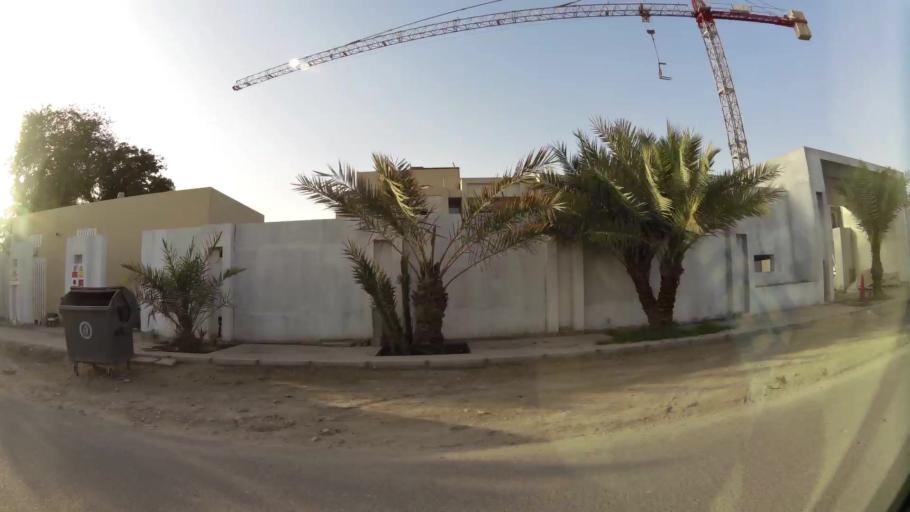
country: QA
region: Baladiyat ar Rayyan
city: Ar Rayyan
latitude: 25.3262
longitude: 51.4513
